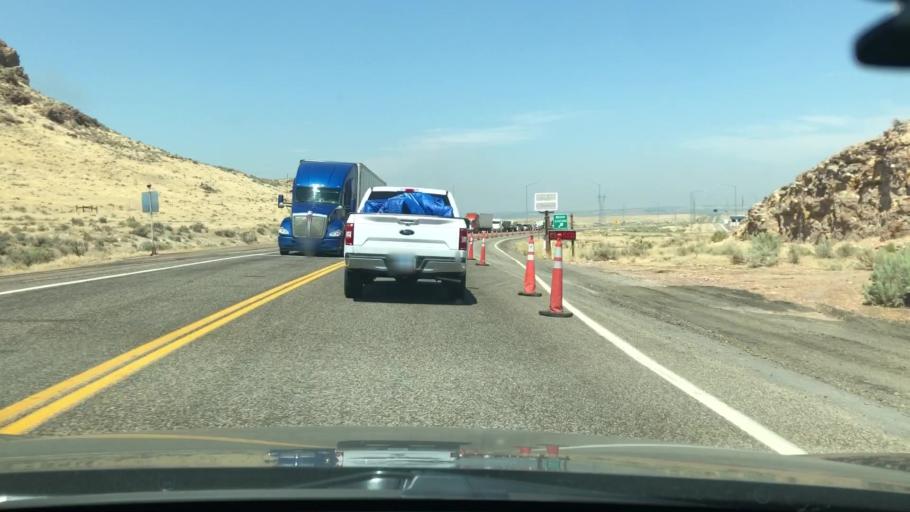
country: US
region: Idaho
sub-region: Owyhee County
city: Marsing
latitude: 43.4609
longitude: -116.8664
